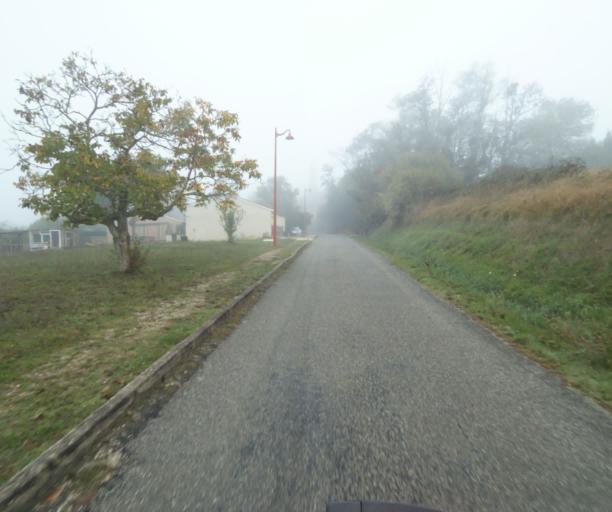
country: FR
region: Midi-Pyrenees
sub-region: Departement du Tarn-et-Garonne
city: Nohic
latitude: 43.9218
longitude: 1.4715
